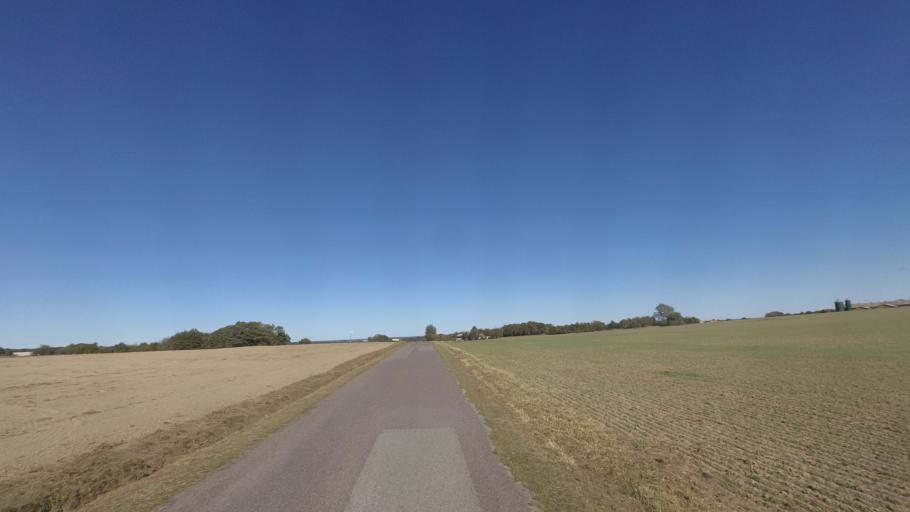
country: DK
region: Capital Region
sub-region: Bornholm Kommune
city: Nexo
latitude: 55.1180
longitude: 15.0456
